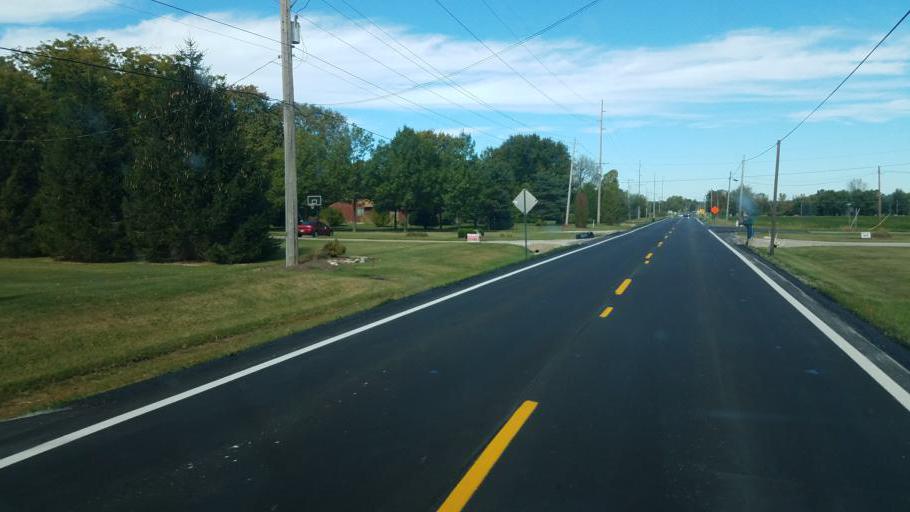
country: US
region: Ohio
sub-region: Erie County
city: Huron
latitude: 41.3603
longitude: -82.4943
